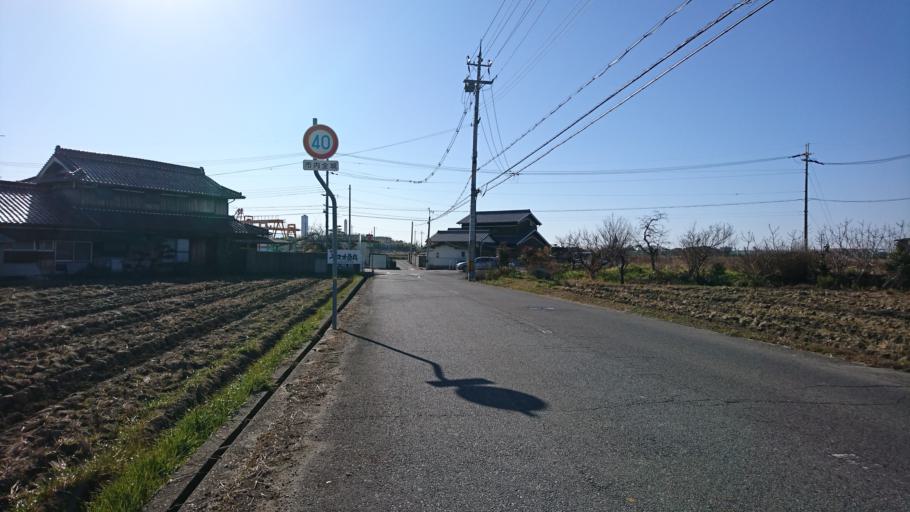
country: JP
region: Hyogo
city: Miki
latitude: 34.7180
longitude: 134.9611
